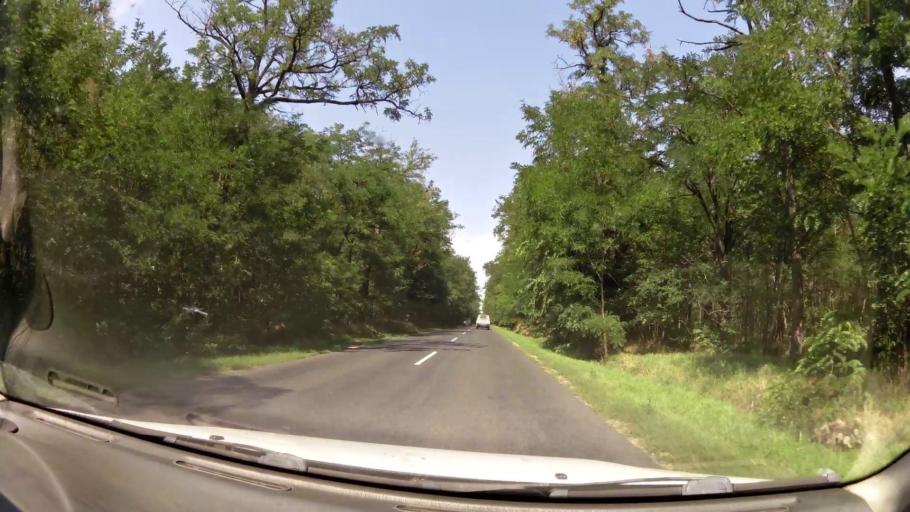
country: HU
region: Pest
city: Tapioszecso
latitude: 47.4306
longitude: 19.6028
